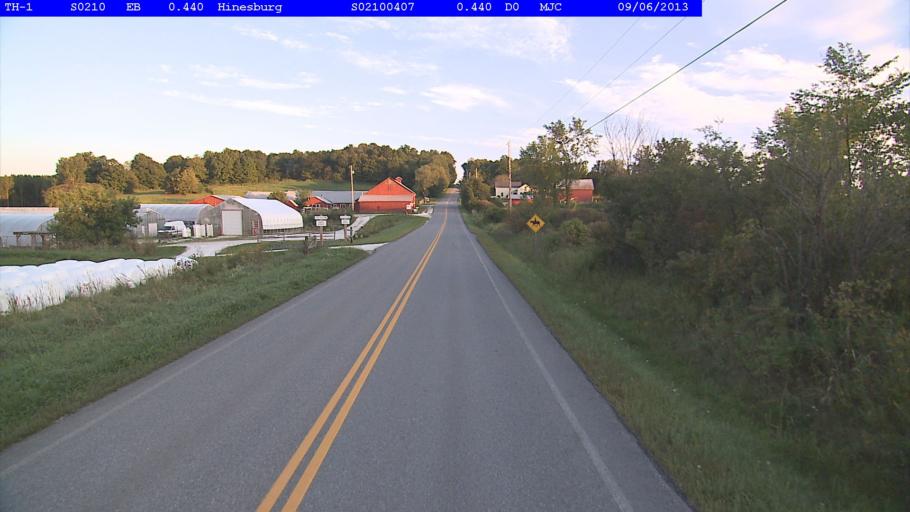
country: US
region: Vermont
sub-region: Chittenden County
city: Hinesburg
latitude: 44.3575
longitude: -73.1567
